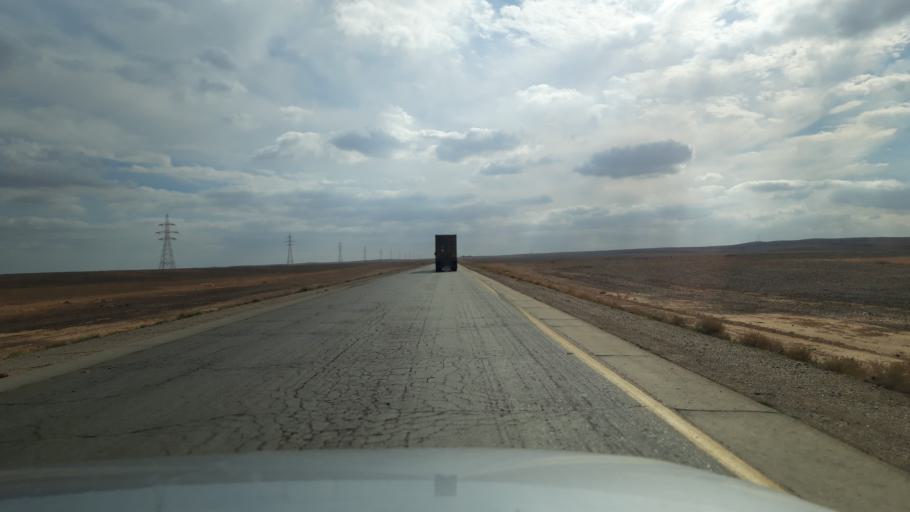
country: JO
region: Amman
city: Al Azraq ash Shamali
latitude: 31.7692
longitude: 36.5616
